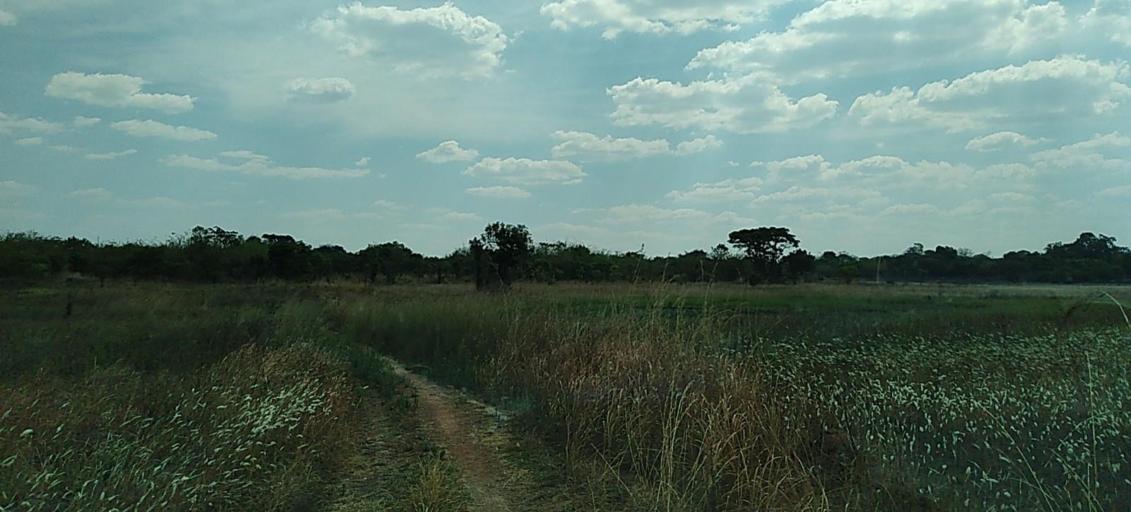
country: ZM
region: Copperbelt
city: Chililabombwe
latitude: -12.3345
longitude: 27.7838
